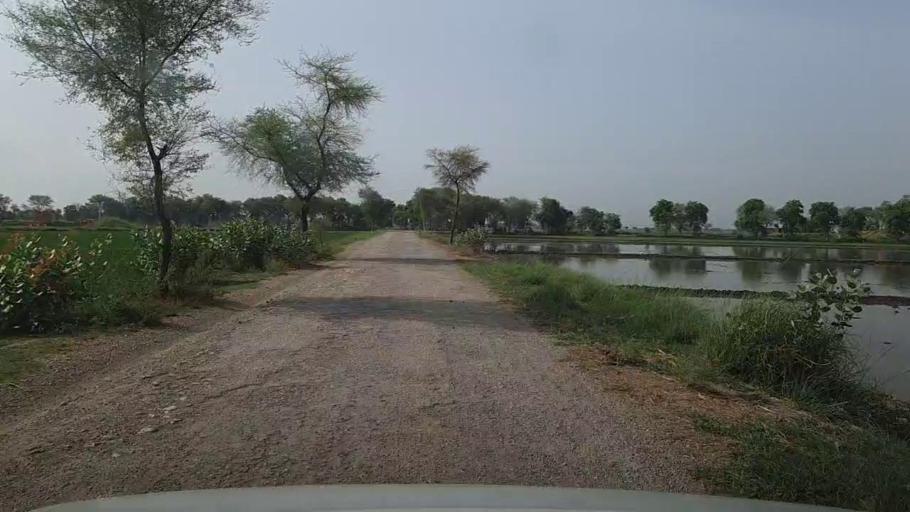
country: PK
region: Sindh
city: Mehar
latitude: 27.1058
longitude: 67.8210
